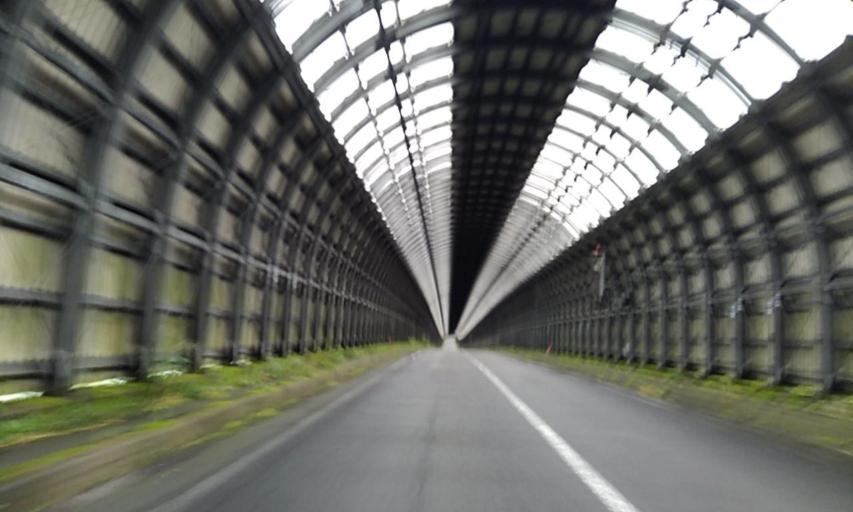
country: JP
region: Hokkaido
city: Abashiri
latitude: 43.6132
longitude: 144.5922
